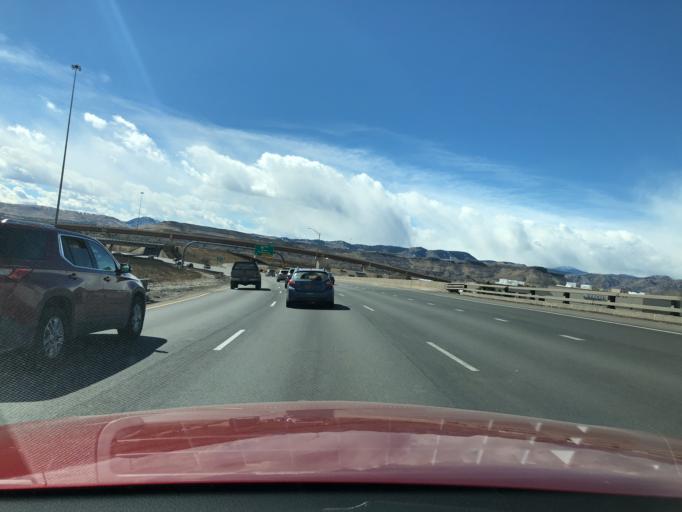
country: US
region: Colorado
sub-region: Jefferson County
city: Applewood
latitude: 39.7785
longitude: -105.1413
